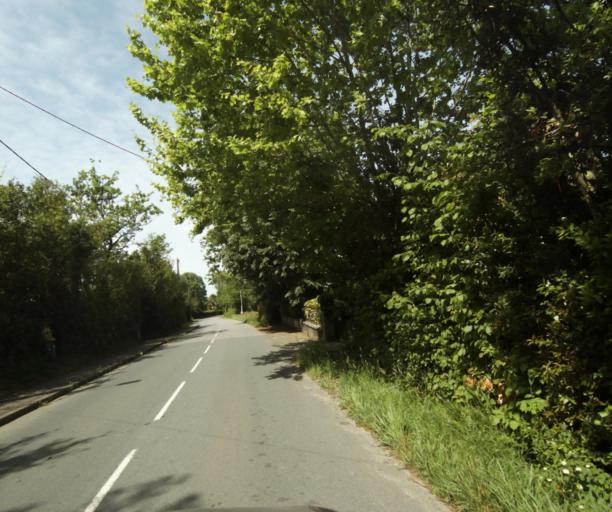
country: FR
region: Aquitaine
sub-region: Departement des Pyrenees-Atlantiques
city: Mouguerre
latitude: 43.4579
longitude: -1.4365
